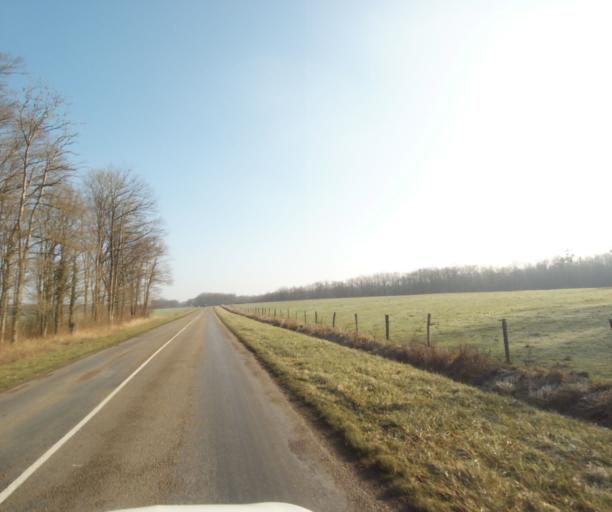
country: FR
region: Champagne-Ardenne
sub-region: Departement de la Haute-Marne
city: Montier-en-Der
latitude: 48.4803
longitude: 4.7974
